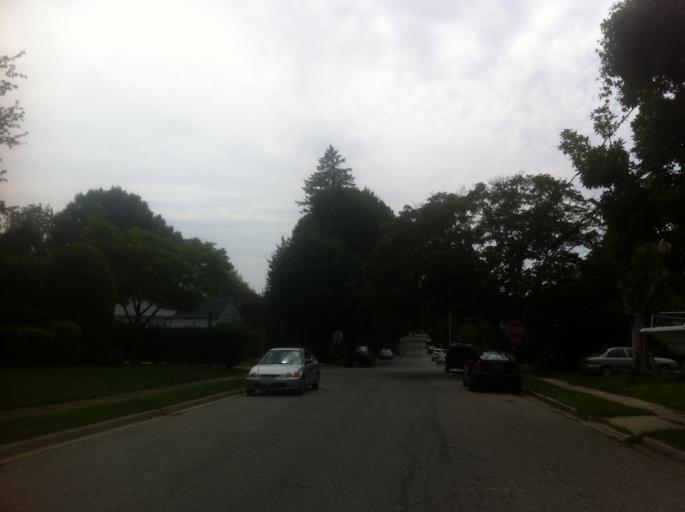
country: US
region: New York
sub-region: Nassau County
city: Locust Valley
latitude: 40.8765
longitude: -73.6045
